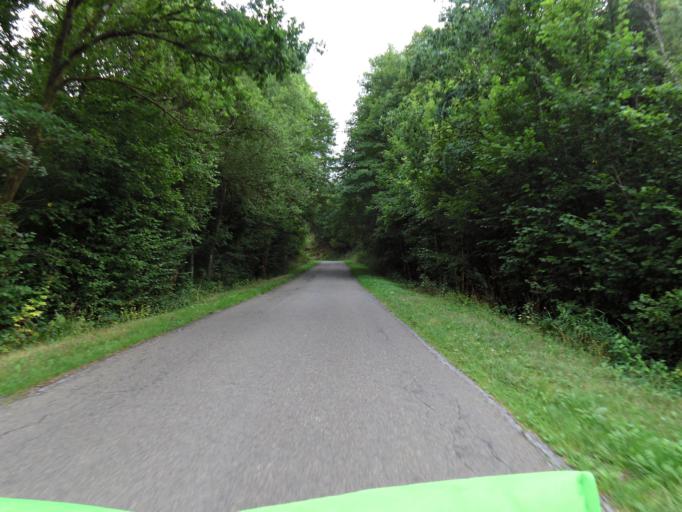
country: BE
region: Wallonia
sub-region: Province de Namur
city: Bievre
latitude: 49.8963
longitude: 5.0018
